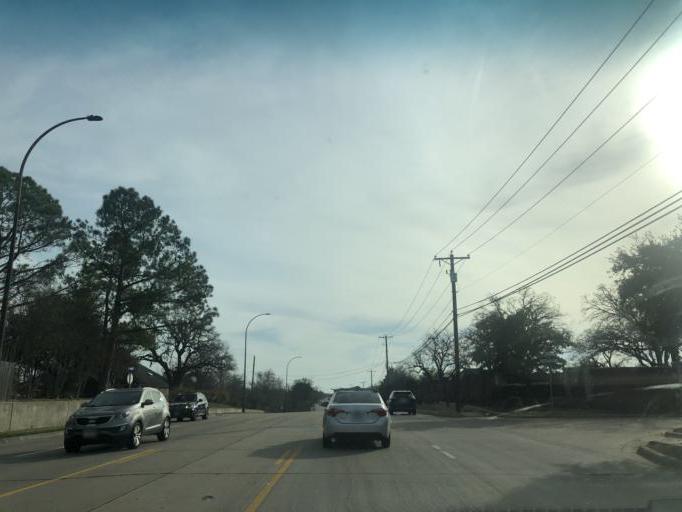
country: US
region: Texas
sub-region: Tarrant County
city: Dalworthington Gardens
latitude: 32.6822
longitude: -97.1495
